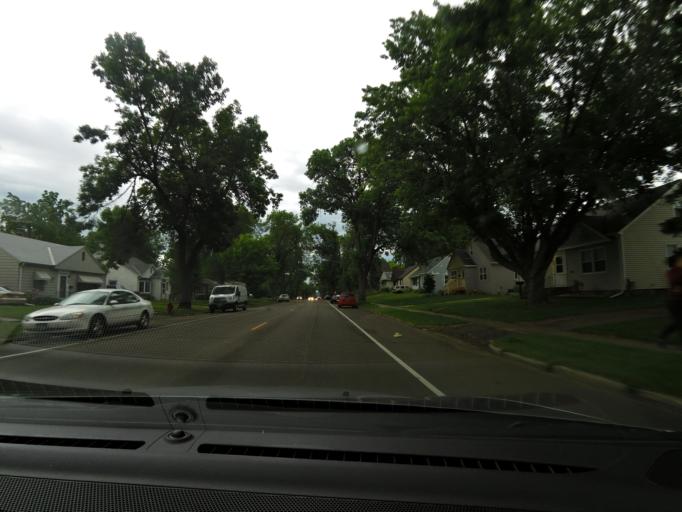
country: US
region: Minnesota
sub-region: Dakota County
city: West Saint Paul
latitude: 44.9124
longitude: -93.0785
